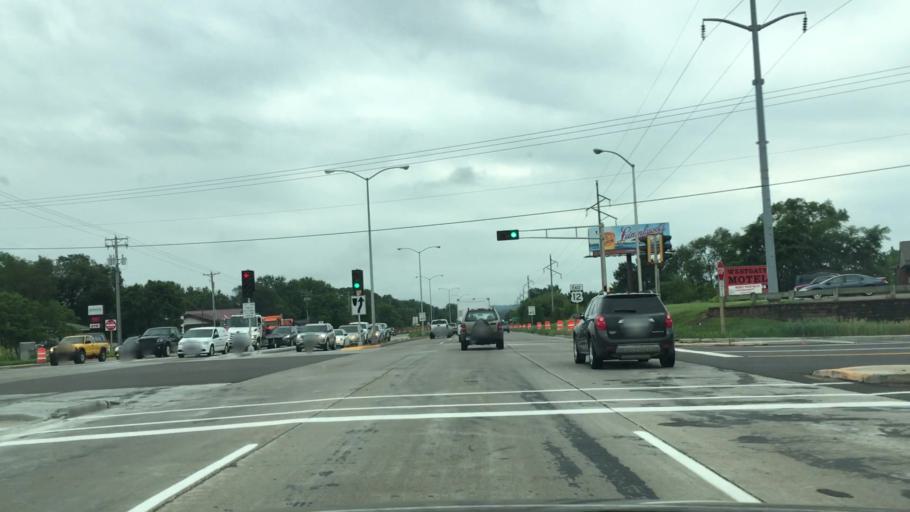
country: US
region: Wisconsin
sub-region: Eau Claire County
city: Eau Claire
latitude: 44.8144
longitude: -91.5398
